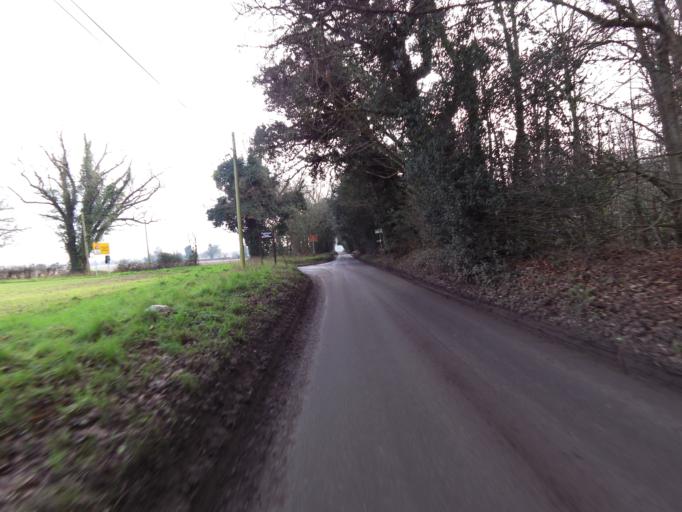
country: GB
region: England
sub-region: Suffolk
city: Woodbridge
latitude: 52.0696
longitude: 1.2946
